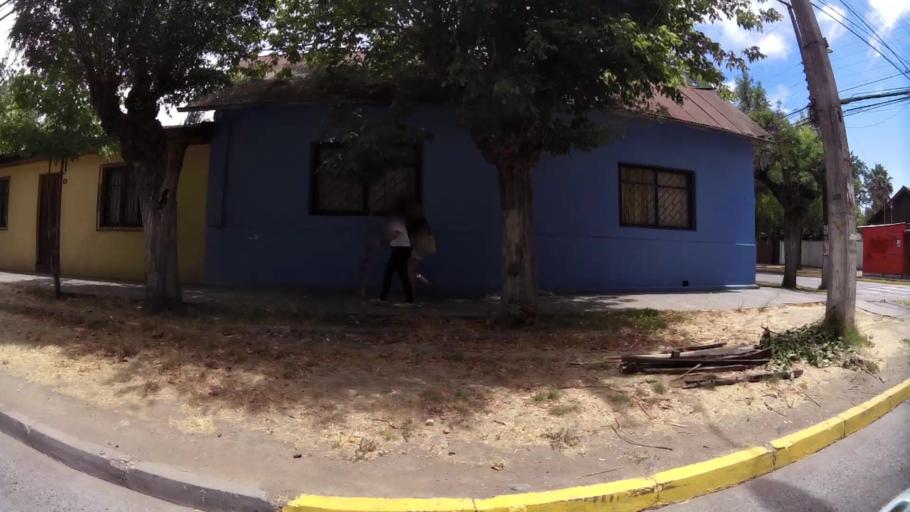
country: CL
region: O'Higgins
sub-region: Provincia de Cachapoal
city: Graneros
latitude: -34.0651
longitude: -70.7273
